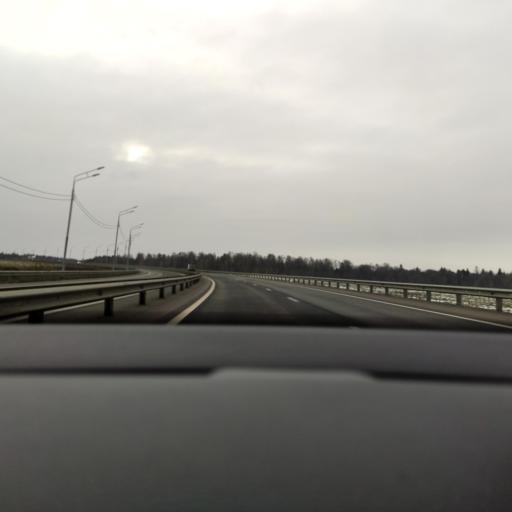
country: RU
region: Moskovskaya
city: Zvenigorod
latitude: 55.6969
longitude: 36.8800
